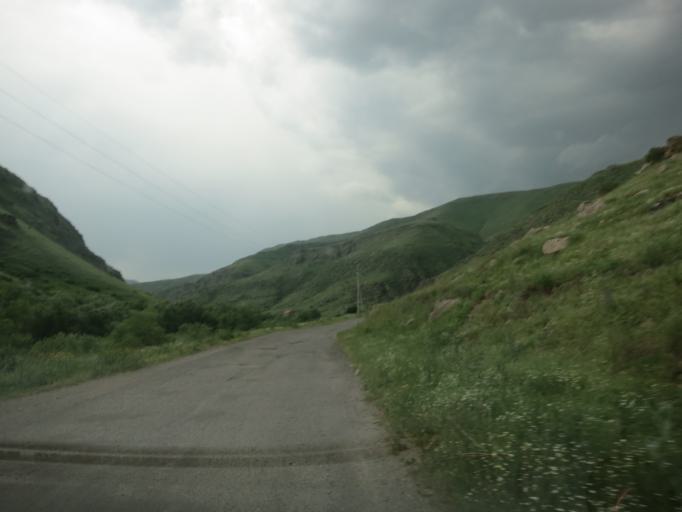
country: TR
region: Ardahan
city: Kurtkale
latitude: 41.3701
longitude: 43.2574
